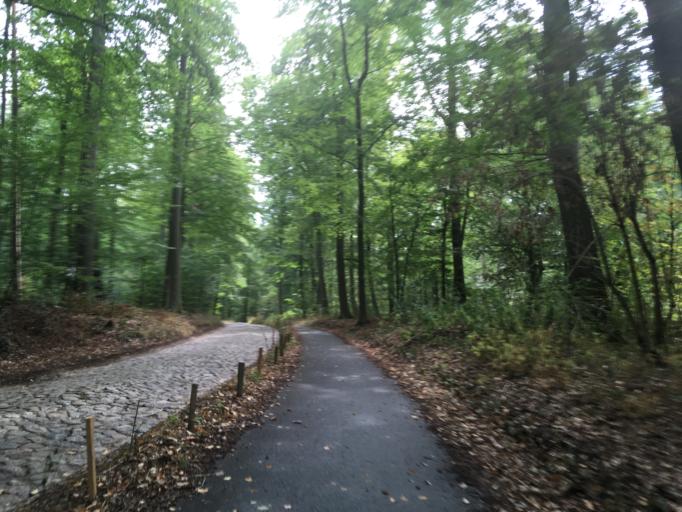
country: DE
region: Brandenburg
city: Chorin
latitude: 52.9123
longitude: 13.8564
